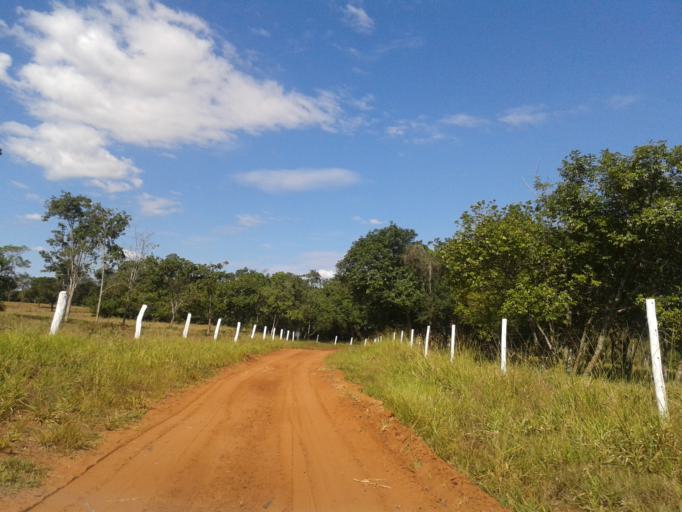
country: BR
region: Minas Gerais
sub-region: Campina Verde
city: Campina Verde
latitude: -19.3852
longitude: -49.7420
